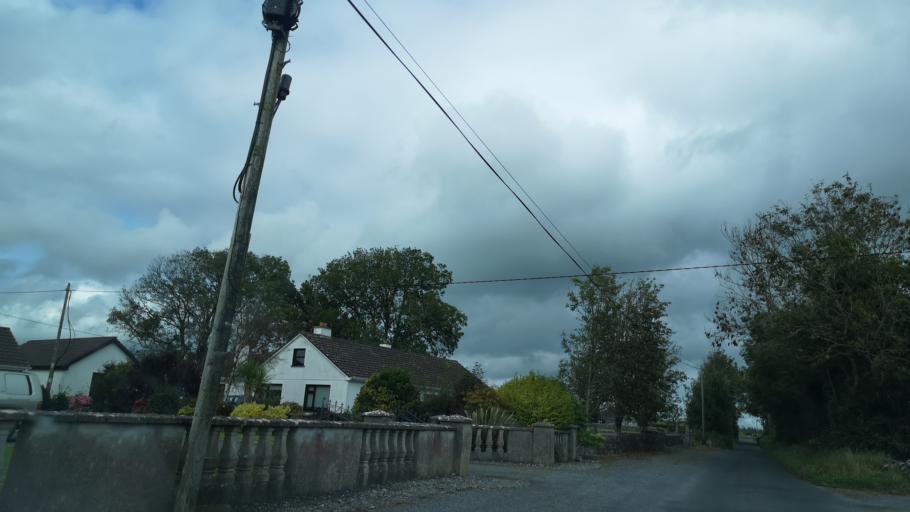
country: IE
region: Connaught
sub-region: County Galway
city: Athenry
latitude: 53.2765
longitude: -8.6718
